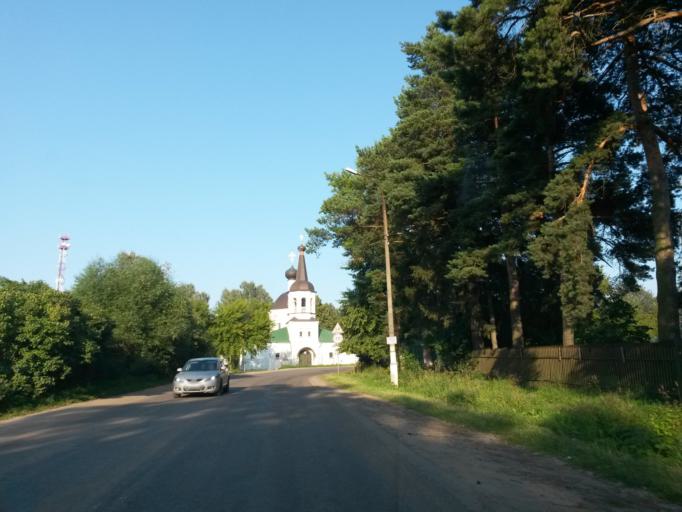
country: RU
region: Moskovskaya
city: Lyubuchany
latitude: 55.2500
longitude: 37.6215
